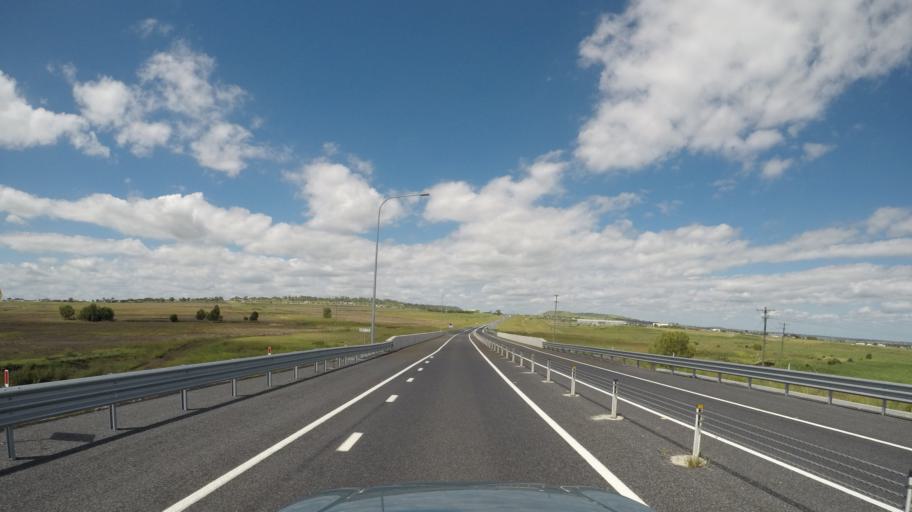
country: AU
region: Queensland
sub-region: Toowoomba
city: Wilsonton Heights
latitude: -27.5312
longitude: 151.8556
